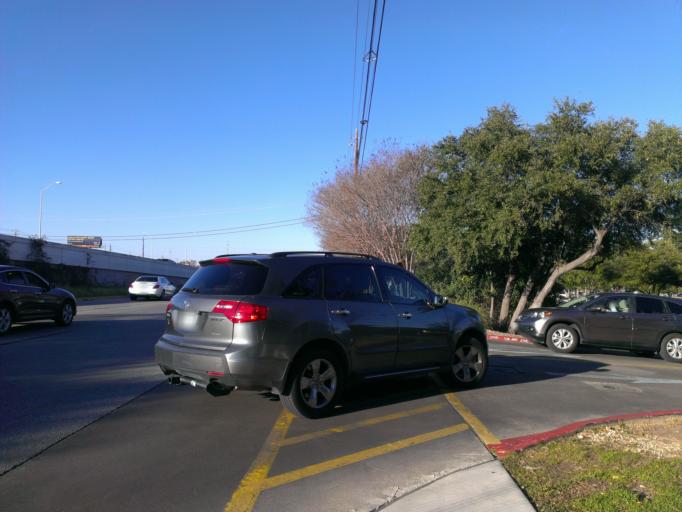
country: US
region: Texas
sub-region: Williamson County
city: Jollyville
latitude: 30.3958
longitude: -97.7458
